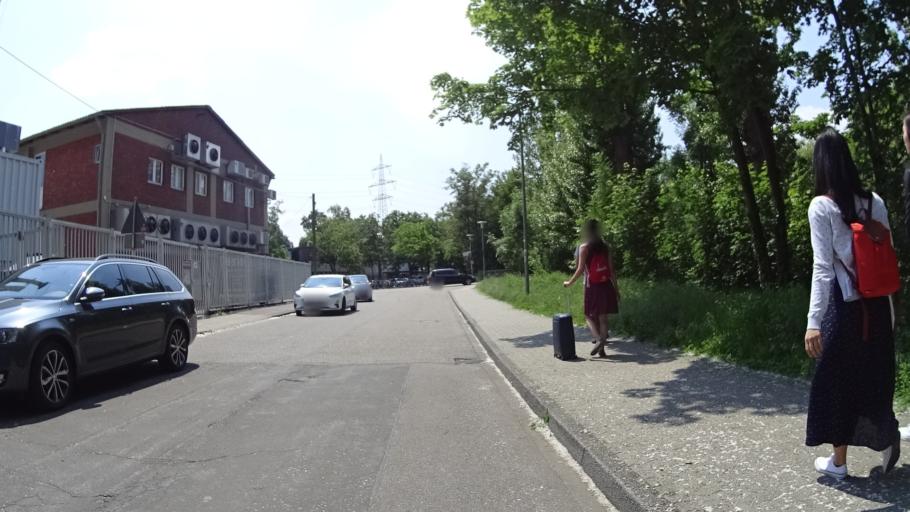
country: DE
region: Baden-Wuerttemberg
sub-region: Karlsruhe Region
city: Karlsruhe
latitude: 49.0139
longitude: 8.3469
